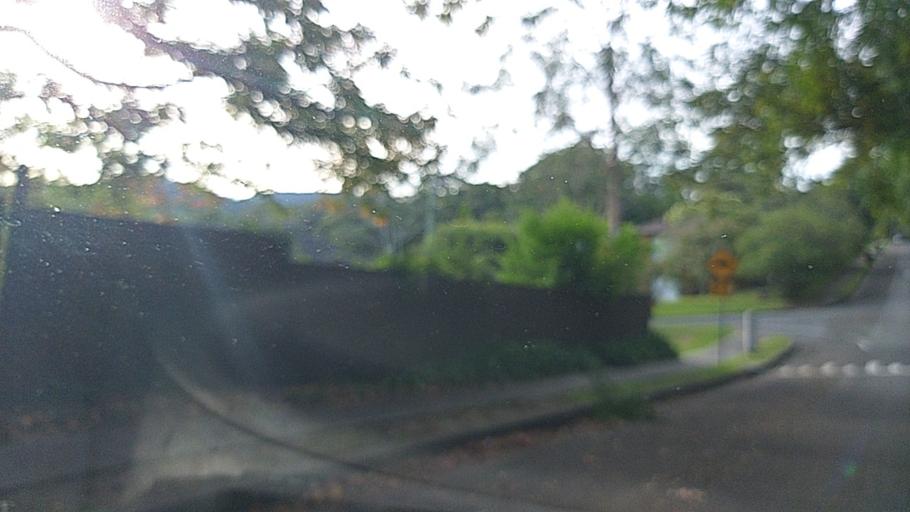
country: AU
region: New South Wales
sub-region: Wollongong
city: Mount Keira
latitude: -34.4309
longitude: 150.8534
